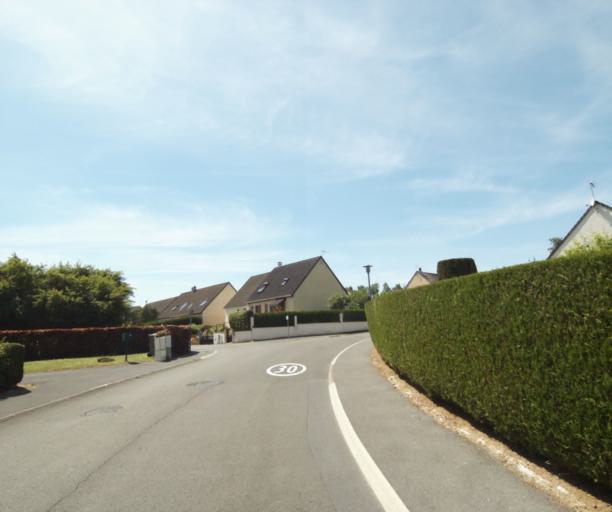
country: FR
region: Champagne-Ardenne
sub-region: Departement des Ardennes
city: Prix-les-Mezieres
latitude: 49.7511
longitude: 4.7057
